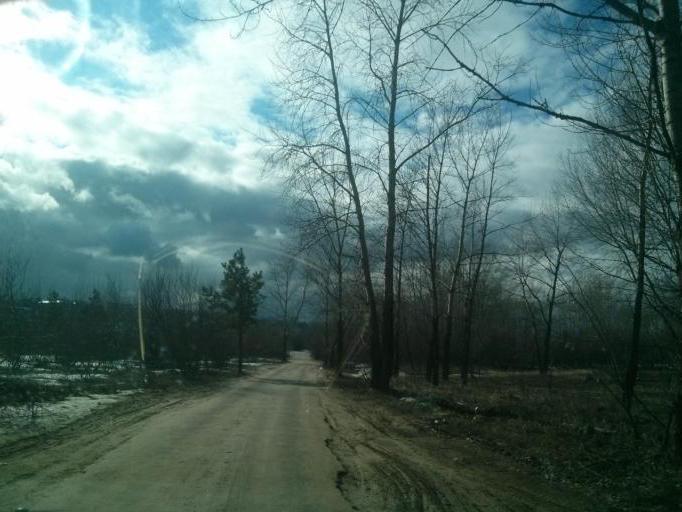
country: RU
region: Nizjnij Novgorod
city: Bor
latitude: 56.3291
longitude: 44.0525
